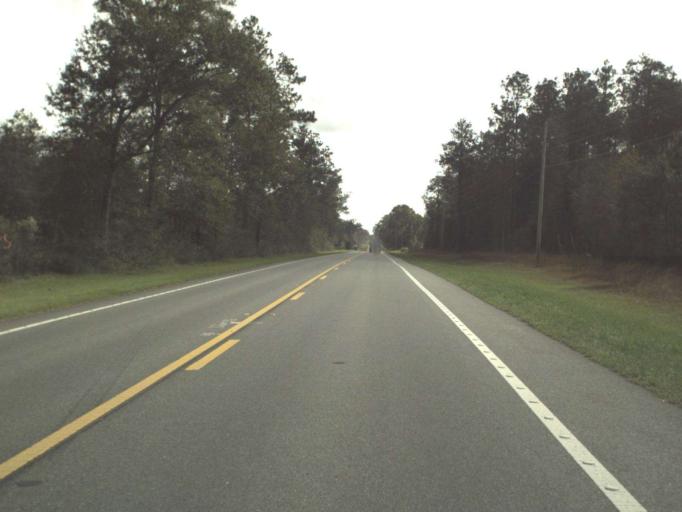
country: US
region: Alabama
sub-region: Escambia County
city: East Brewton
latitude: 30.9563
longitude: -87.0427
